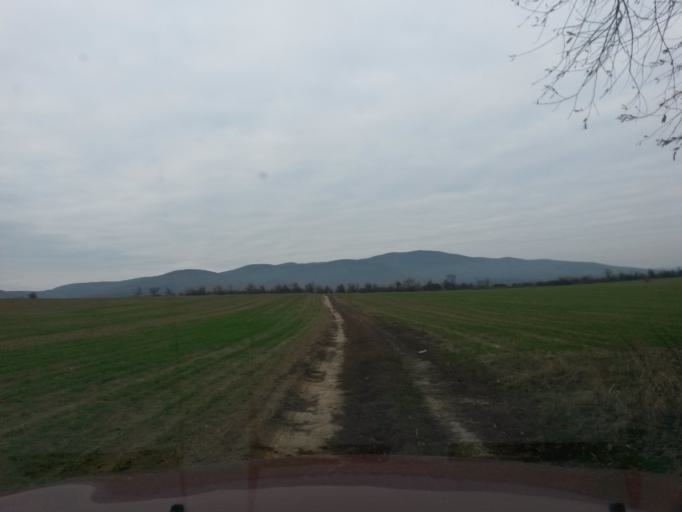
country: SK
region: Kosicky
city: Secovce
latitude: 48.6427
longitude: 21.5935
